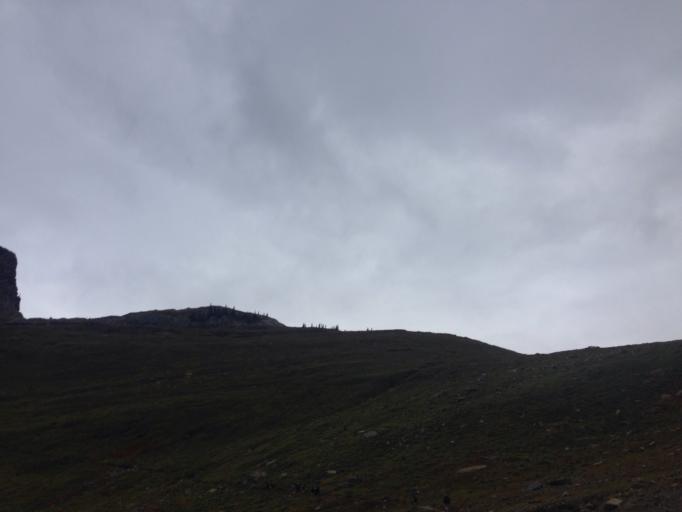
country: US
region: Montana
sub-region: Flathead County
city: Columbia Falls
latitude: 48.7341
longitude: -113.7226
